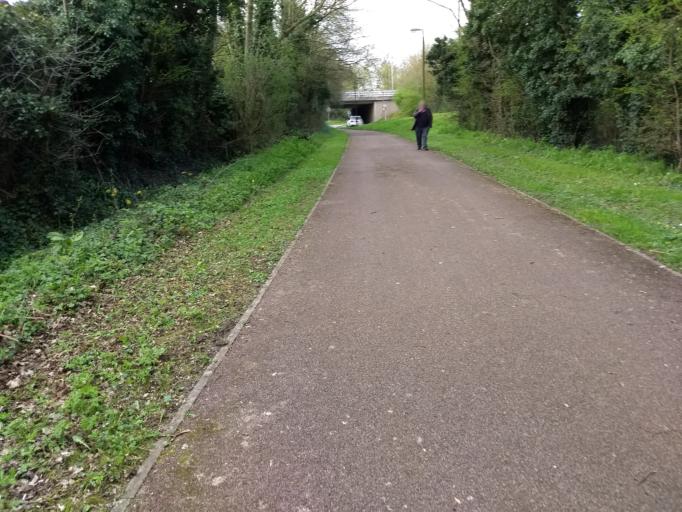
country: GB
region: England
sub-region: Milton Keynes
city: Simpson
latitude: 52.0249
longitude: -0.7206
